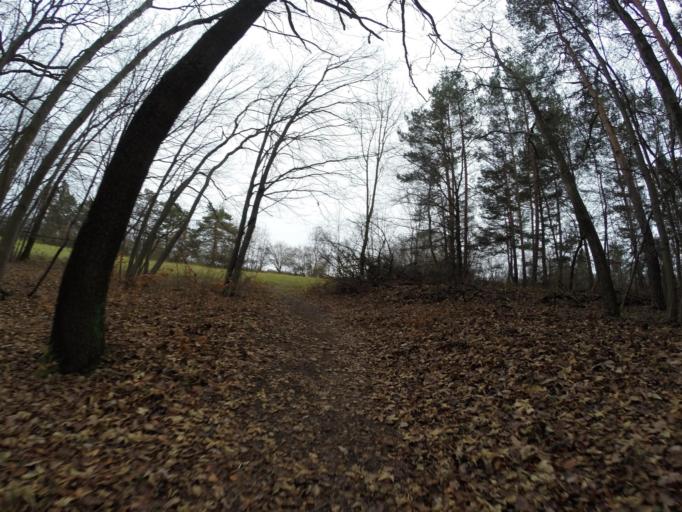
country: DE
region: Thuringia
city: Jena
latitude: 50.9161
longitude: 11.6196
